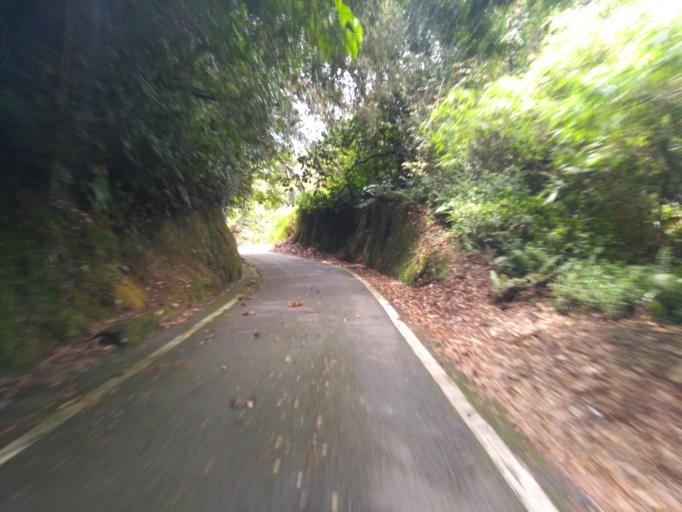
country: MY
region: Pahang
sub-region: Cameron Highlands
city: Tanah Rata
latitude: 4.4842
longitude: 101.3845
